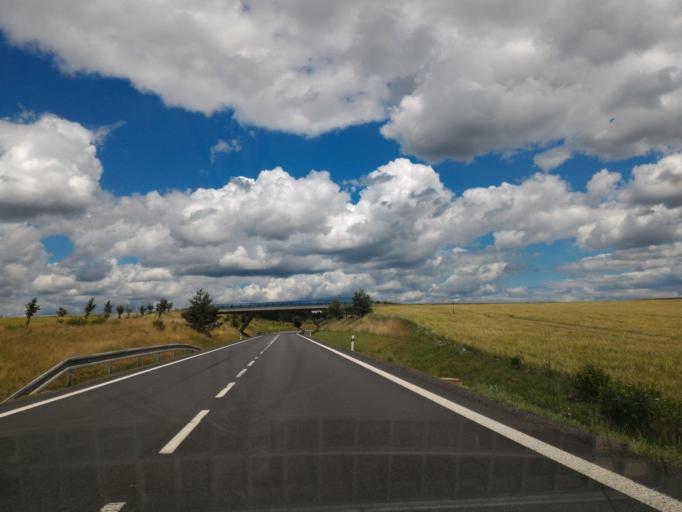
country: CZ
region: Vysocina
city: Bohdalov
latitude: 49.4831
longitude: 15.8661
